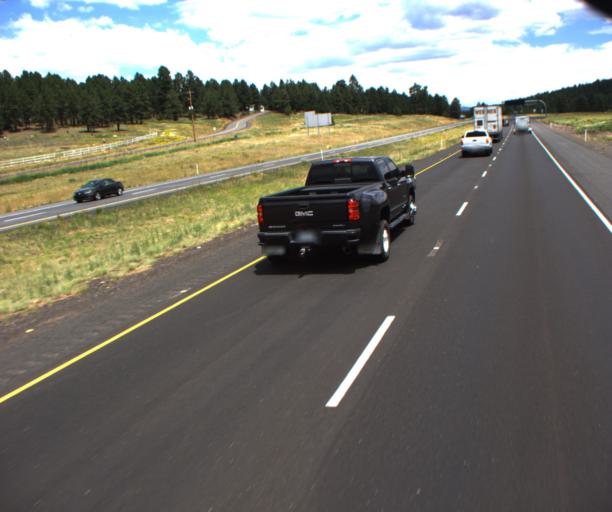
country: US
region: Arizona
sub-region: Coconino County
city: Kachina Village
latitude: 35.0984
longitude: -111.6830
